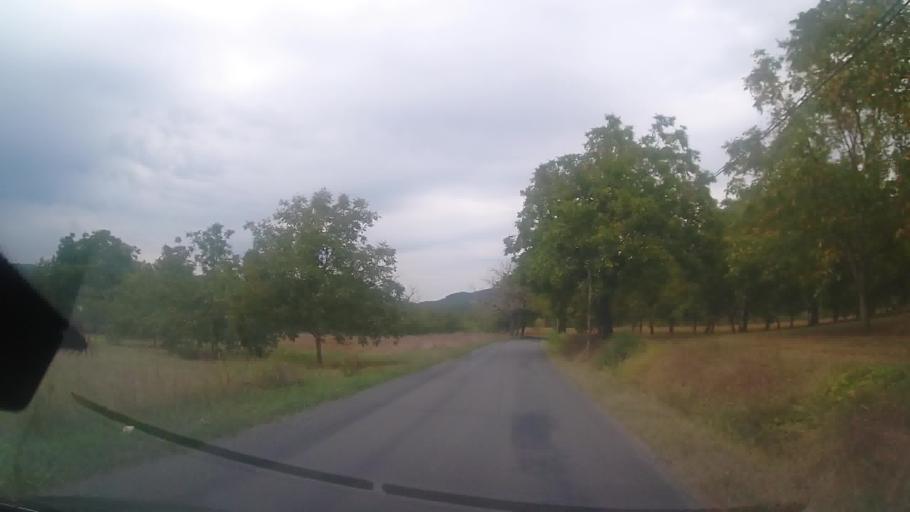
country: FR
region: Aquitaine
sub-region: Departement de la Dordogne
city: Eyvigues-et-Eybenes
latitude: 44.8513
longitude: 1.3647
